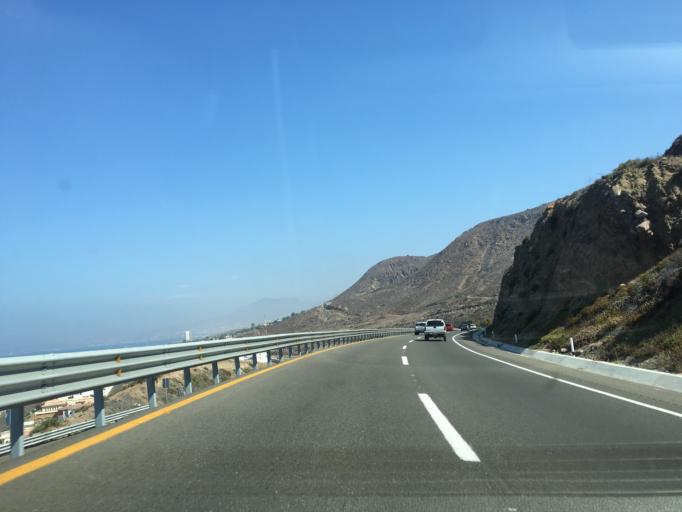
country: MX
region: Baja California
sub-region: Playas de Rosarito
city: Santa Anita
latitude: 32.1537
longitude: -116.8943
